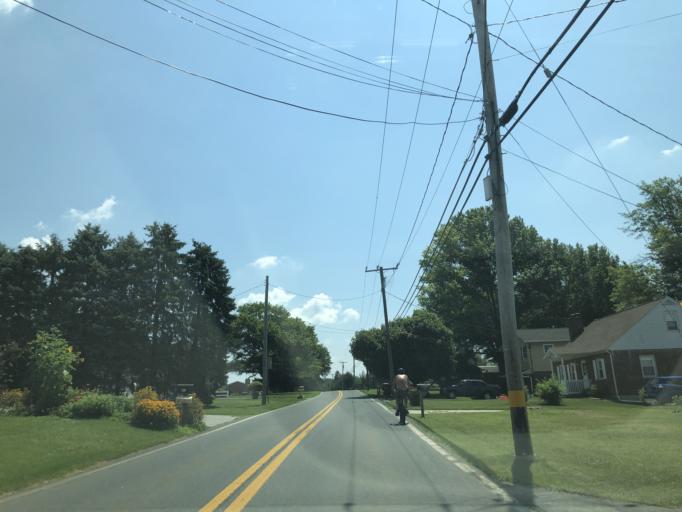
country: US
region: Maryland
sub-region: Carroll County
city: Westminster
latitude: 39.5398
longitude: -76.9800
